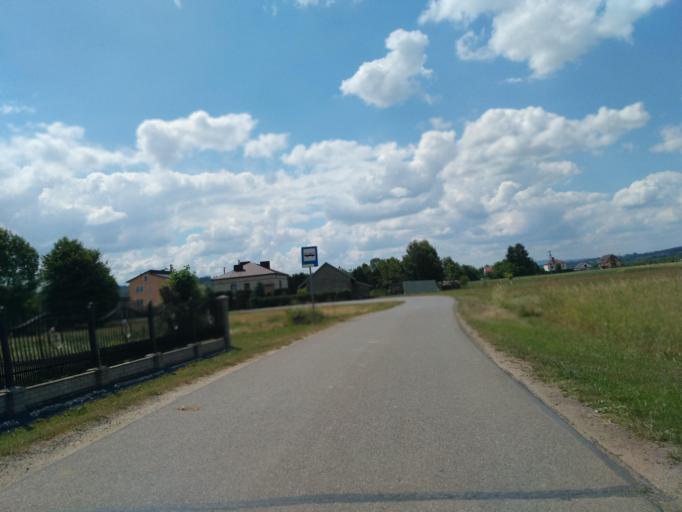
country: PL
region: Subcarpathian Voivodeship
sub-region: Powiat jasielski
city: Kolaczyce
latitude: 49.8074
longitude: 21.4160
